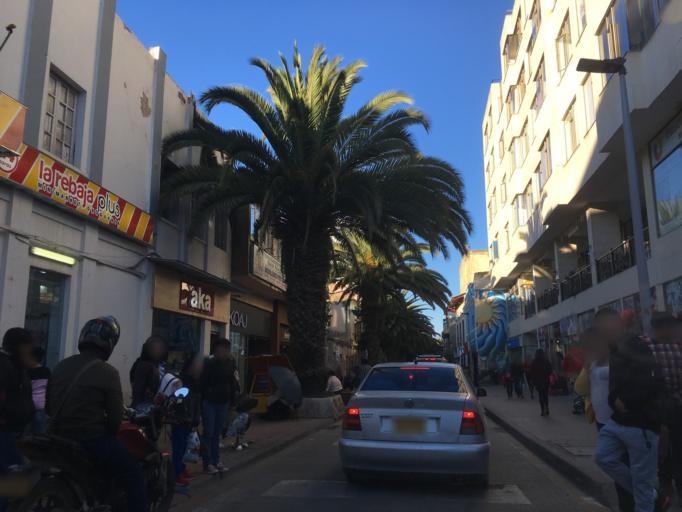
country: CO
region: Boyaca
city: Sogamoso
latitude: 5.7155
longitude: -72.9279
